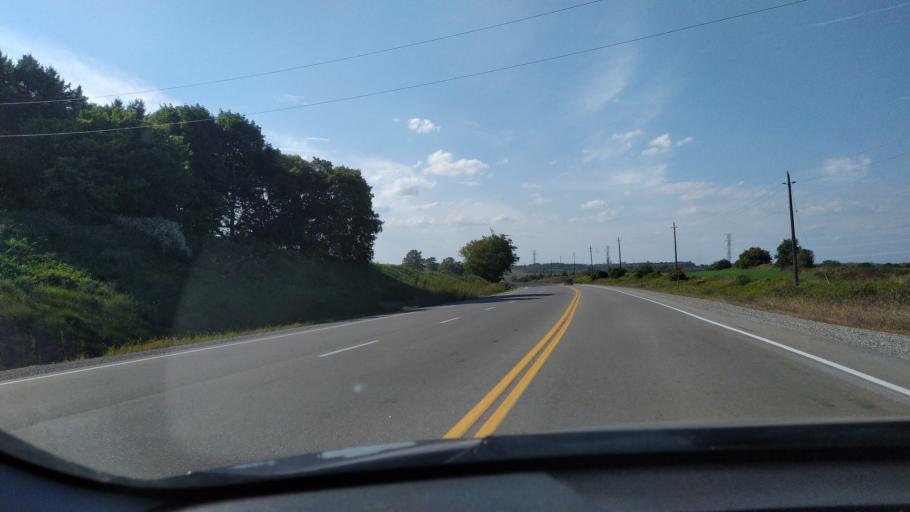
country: CA
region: Ontario
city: Ingersoll
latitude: 43.0643
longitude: -80.8392
